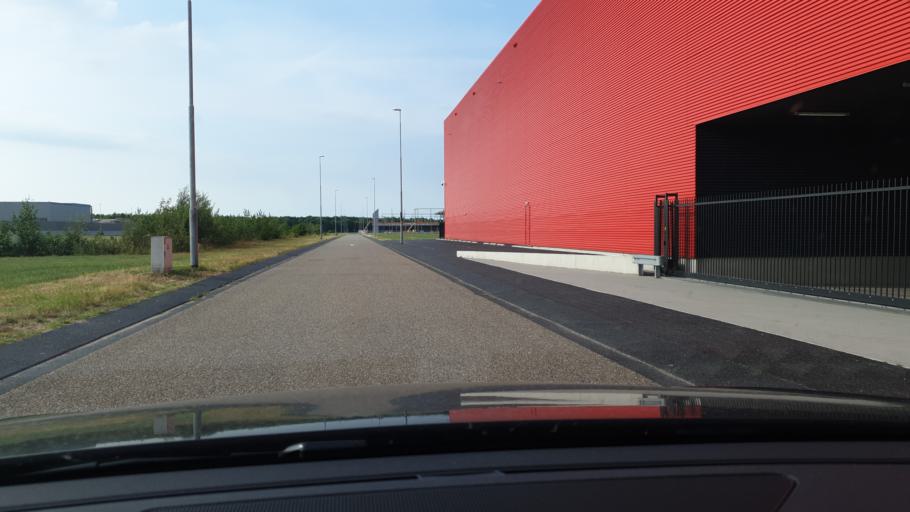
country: NL
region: North Brabant
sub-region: Gemeente Veldhoven
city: Oerle
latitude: 51.4377
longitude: 5.3840
